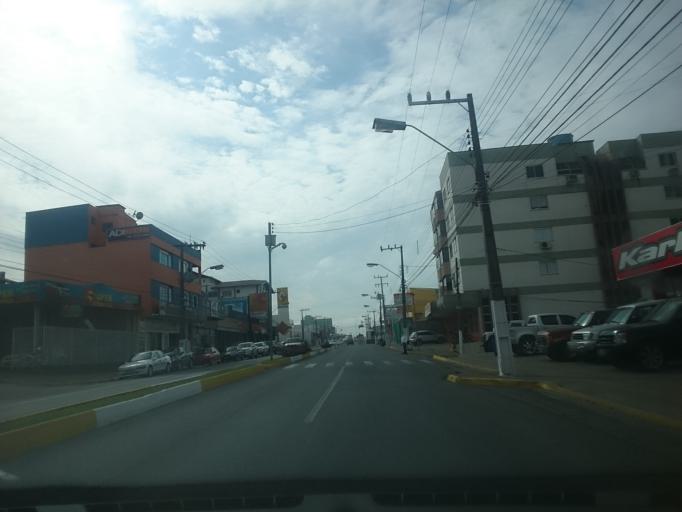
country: BR
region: Santa Catarina
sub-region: Lages
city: Lages
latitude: -27.8116
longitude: -50.3075
